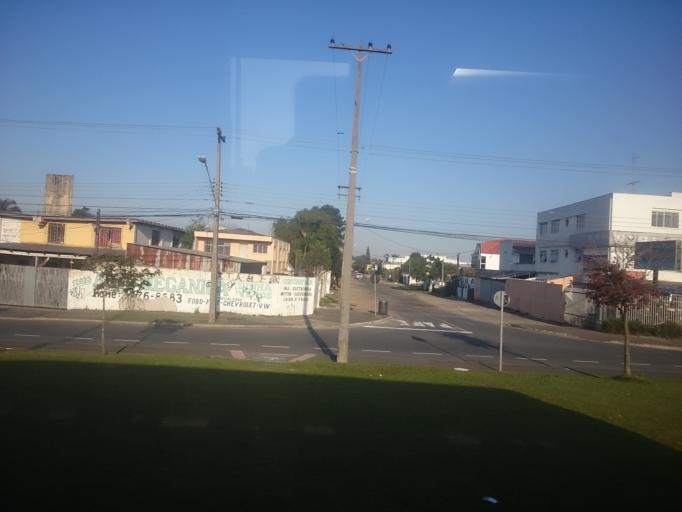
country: BR
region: Parana
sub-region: Curitiba
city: Curitiba
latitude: -25.5045
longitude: -49.2824
